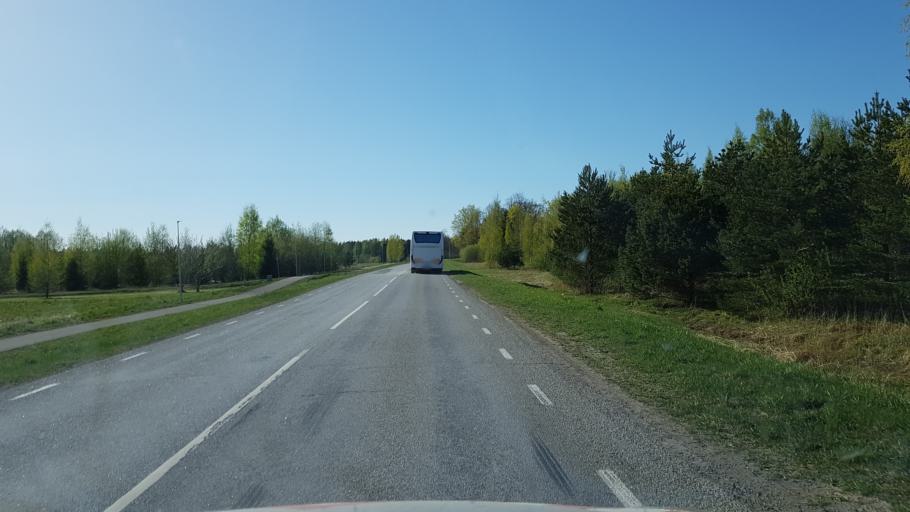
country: EE
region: Paernumaa
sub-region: Paikuse vald
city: Paikuse
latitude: 58.3591
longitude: 24.6567
